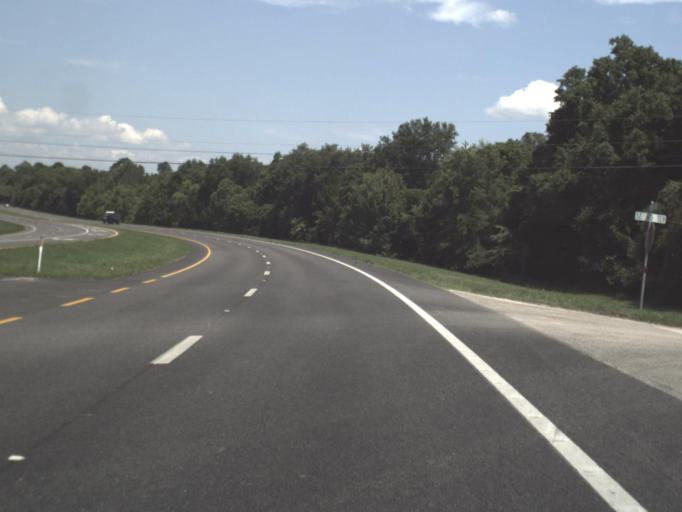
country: US
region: Florida
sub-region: Alachua County
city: Gainesville
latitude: 29.6129
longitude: -82.2539
